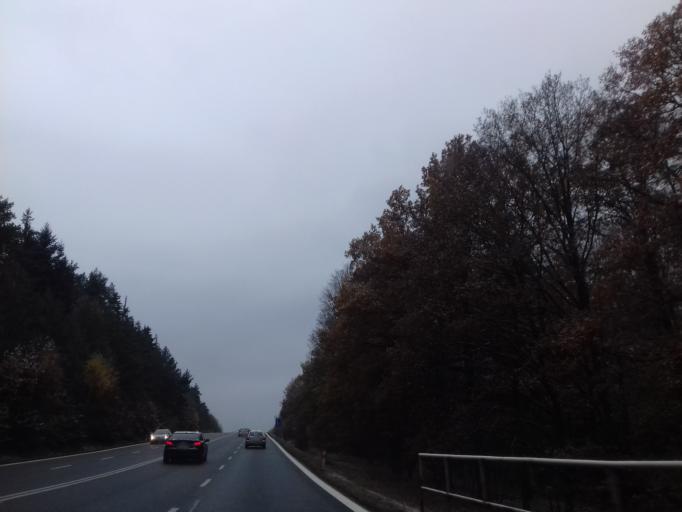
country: CZ
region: Plzensky
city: Holysov
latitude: 49.6072
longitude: 13.1208
